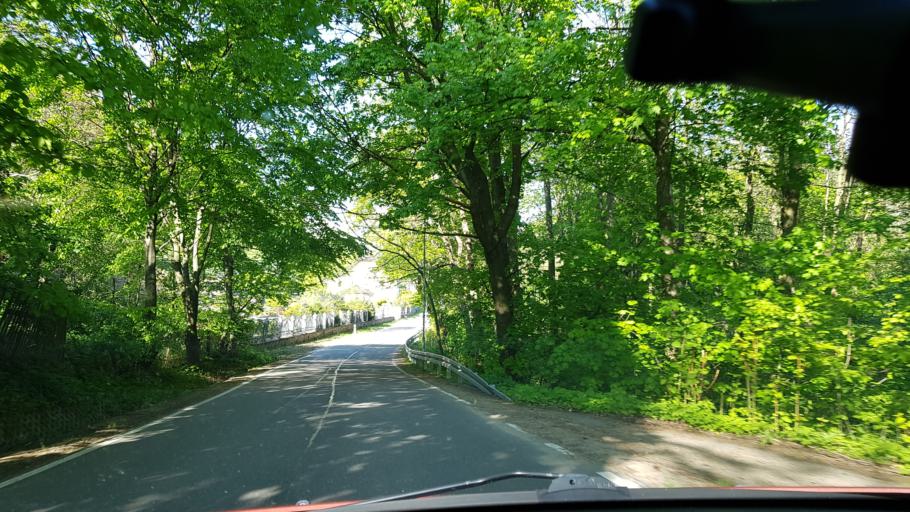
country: PL
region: Lower Silesian Voivodeship
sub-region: Powiat zabkowicki
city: Budzow
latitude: 50.5703
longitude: 16.6443
